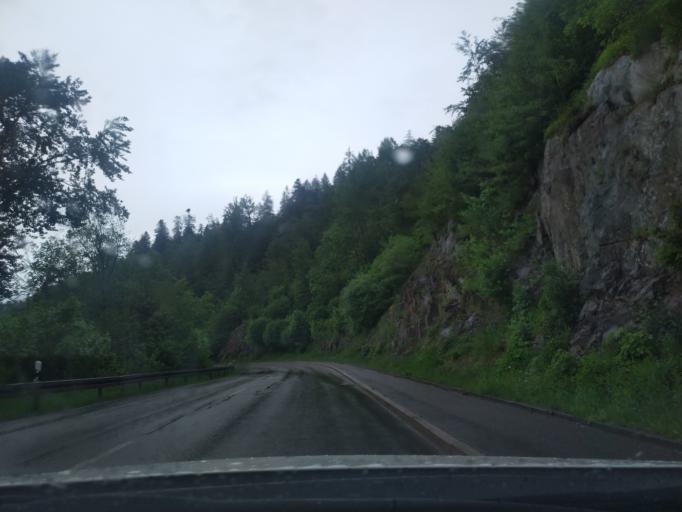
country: DE
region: Baden-Wuerttemberg
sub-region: Freiburg Region
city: Hausern
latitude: 47.7569
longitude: 8.1498
